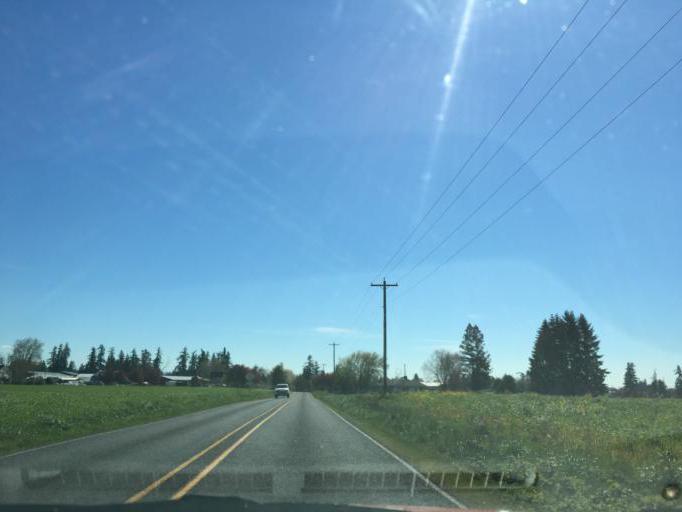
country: US
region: Oregon
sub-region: Marion County
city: Hubbard
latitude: 45.1576
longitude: -122.7227
